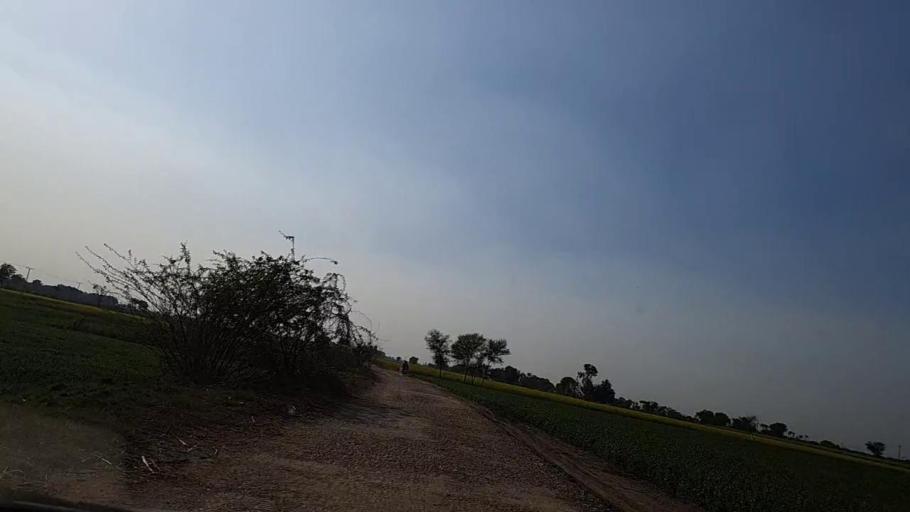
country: PK
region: Sindh
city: Sakrand
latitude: 26.1282
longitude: 68.2629
